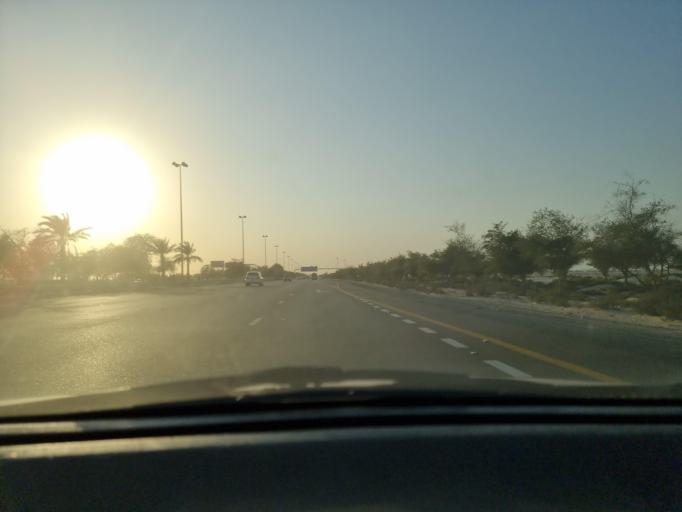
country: AE
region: Abu Dhabi
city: Abu Dhabi
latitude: 24.4125
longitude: 54.6960
